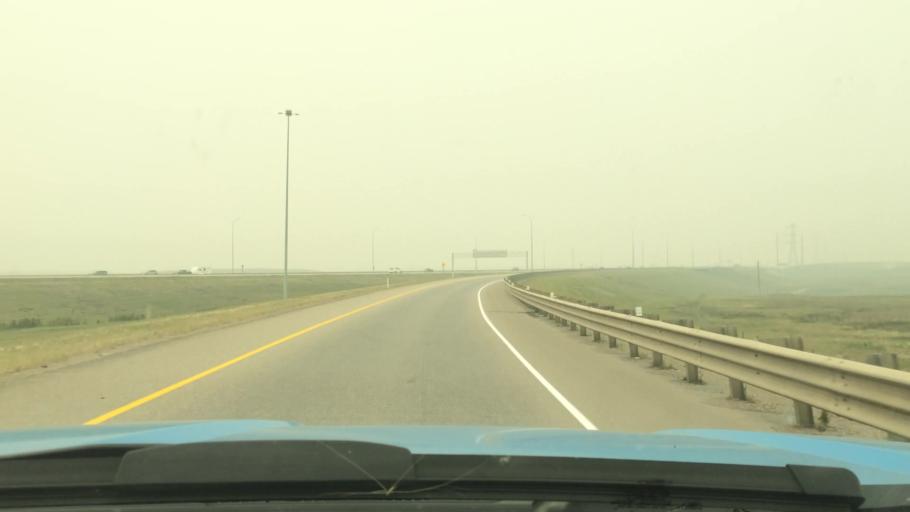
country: CA
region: Alberta
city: Airdrie
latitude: 51.1771
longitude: -114.0086
